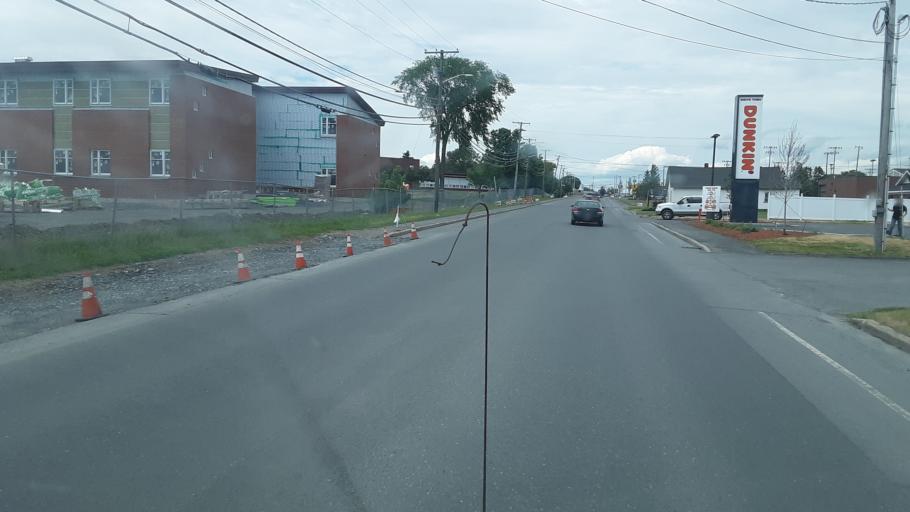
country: US
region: Maine
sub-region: Aroostook County
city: Caribou
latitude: 46.8630
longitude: -68.0048
